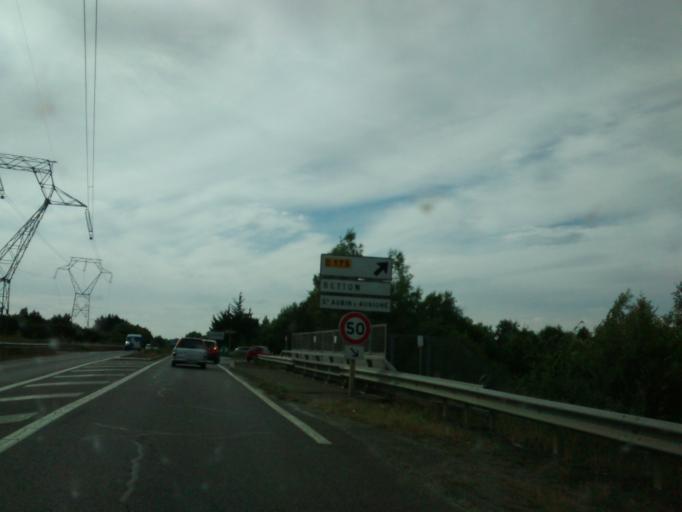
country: FR
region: Brittany
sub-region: Departement d'Ille-et-Vilaine
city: Betton
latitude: 48.1594
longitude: -1.6473
